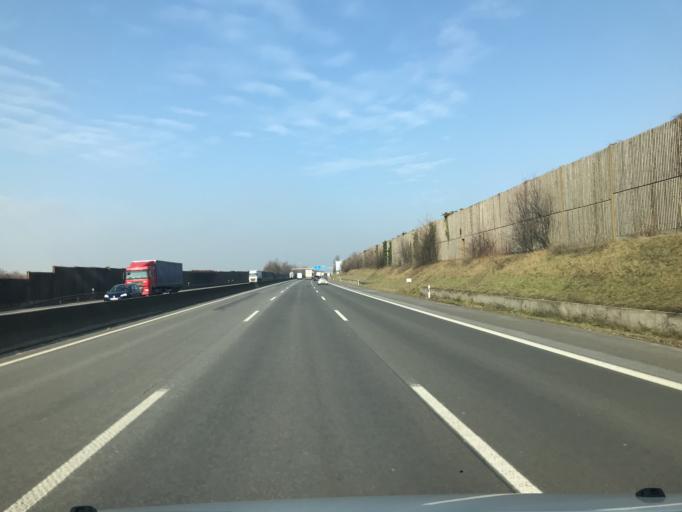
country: DE
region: North Rhine-Westphalia
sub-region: Regierungsbezirk Koln
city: Titz
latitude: 51.0777
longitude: 6.4254
